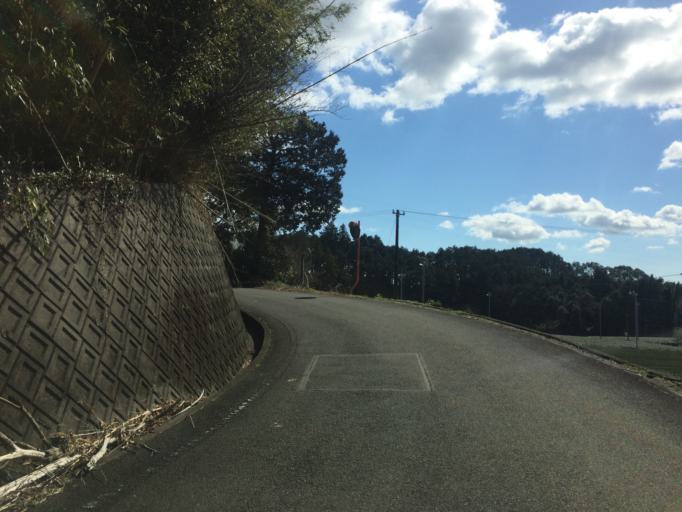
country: JP
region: Shizuoka
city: Shimada
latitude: 34.7669
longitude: 138.1965
